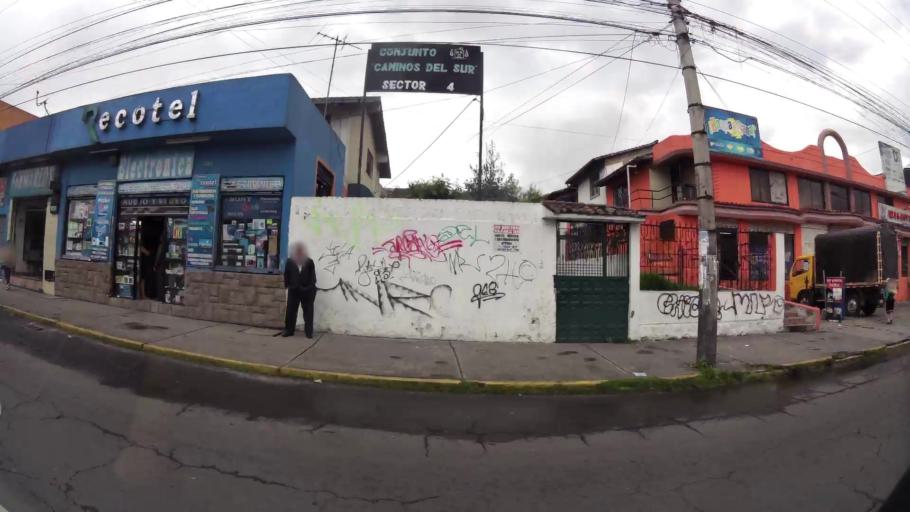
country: EC
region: Pichincha
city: Quito
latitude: -0.2709
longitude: -78.5520
